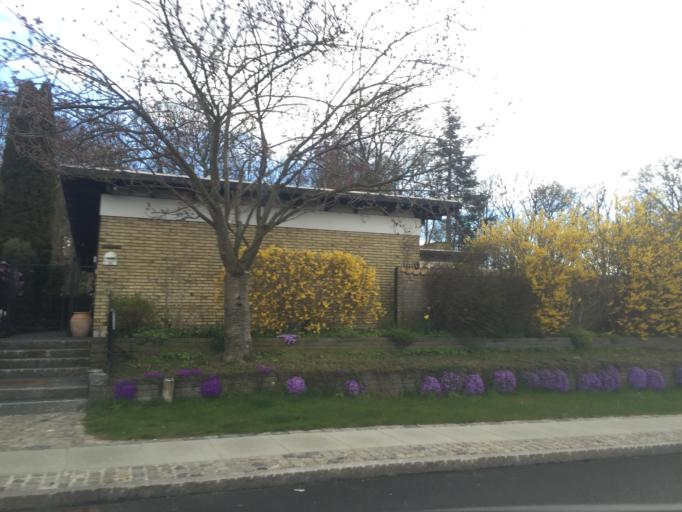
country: DK
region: Capital Region
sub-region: Gentofte Kommune
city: Charlottenlund
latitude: 55.7668
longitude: 12.5602
